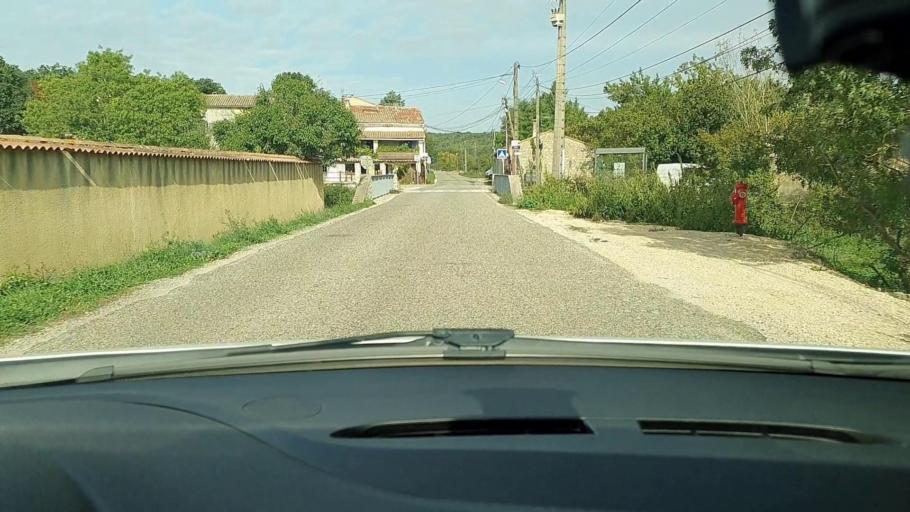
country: FR
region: Languedoc-Roussillon
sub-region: Departement du Gard
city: Saint-Quentin-la-Poterie
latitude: 44.1352
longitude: 4.4004
